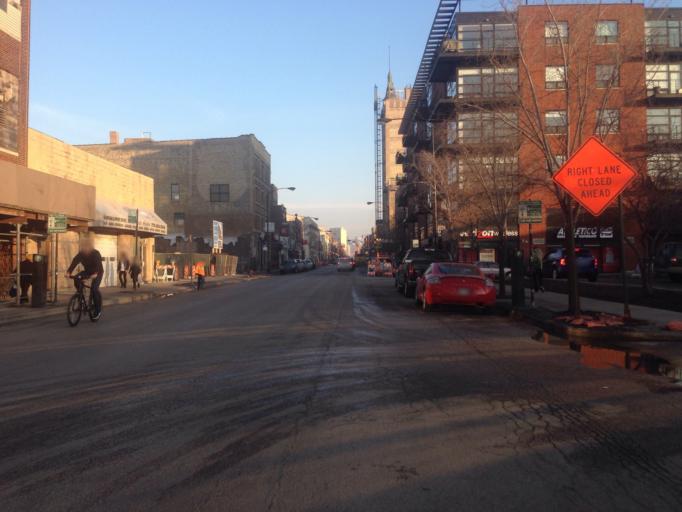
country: US
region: Illinois
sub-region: Cook County
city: Chicago
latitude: 41.9118
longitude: -87.6797
